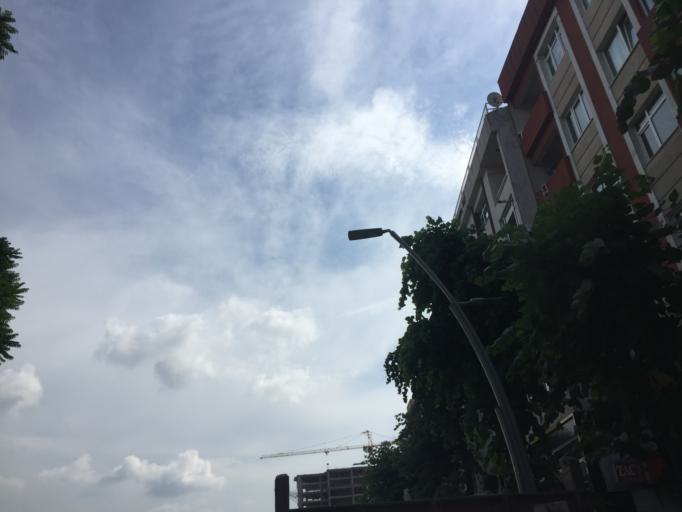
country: TR
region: Istanbul
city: Zeytinburnu
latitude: 40.9967
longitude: 28.9032
